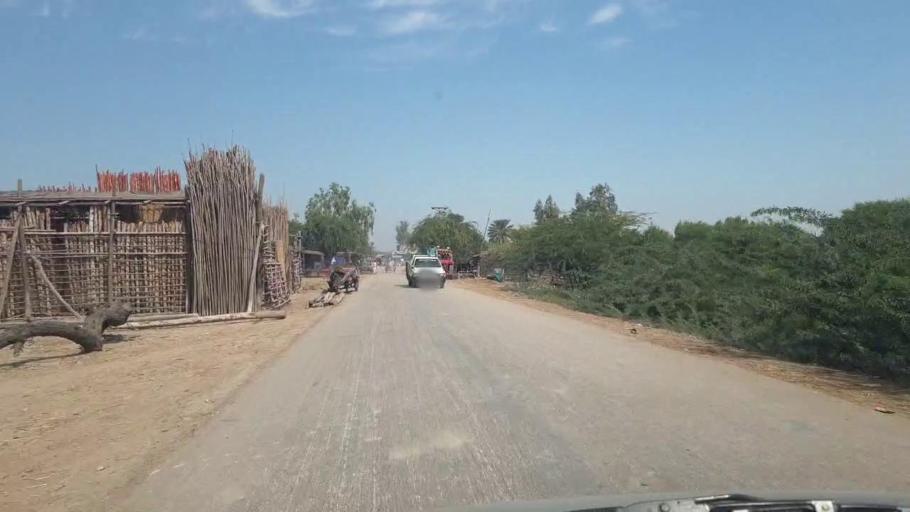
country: PK
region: Sindh
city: Tando Bago
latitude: 24.8921
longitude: 69.0032
